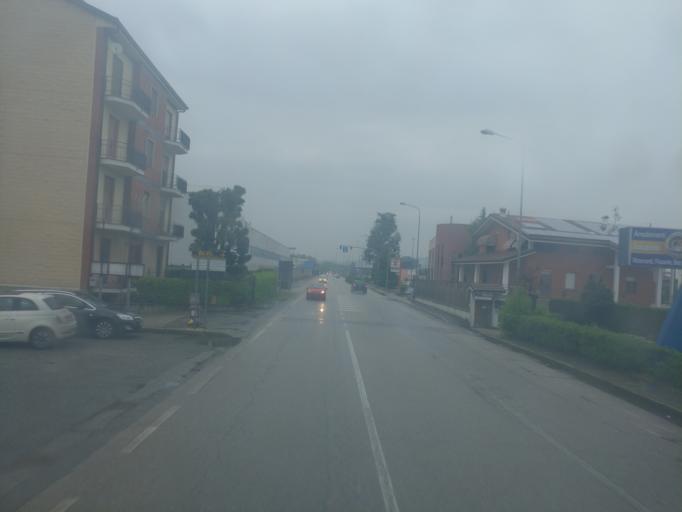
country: IT
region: Piedmont
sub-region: Provincia di Torino
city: La Loggia
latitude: 44.9612
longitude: 7.6679
